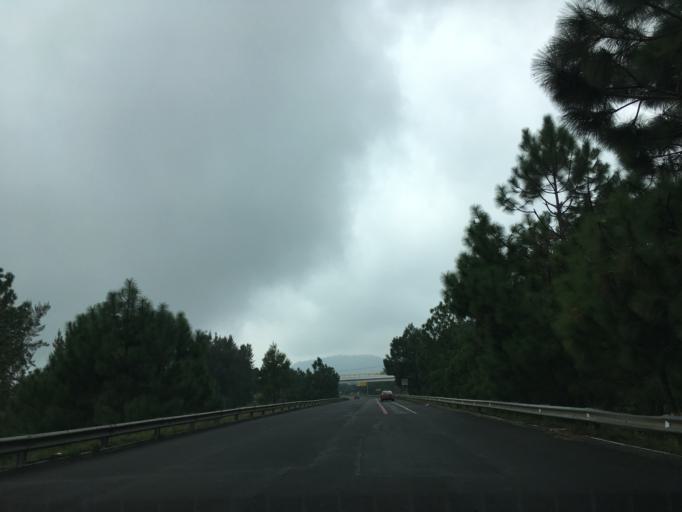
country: MX
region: Michoacan
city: Tingambato
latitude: 19.4471
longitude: -101.8654
